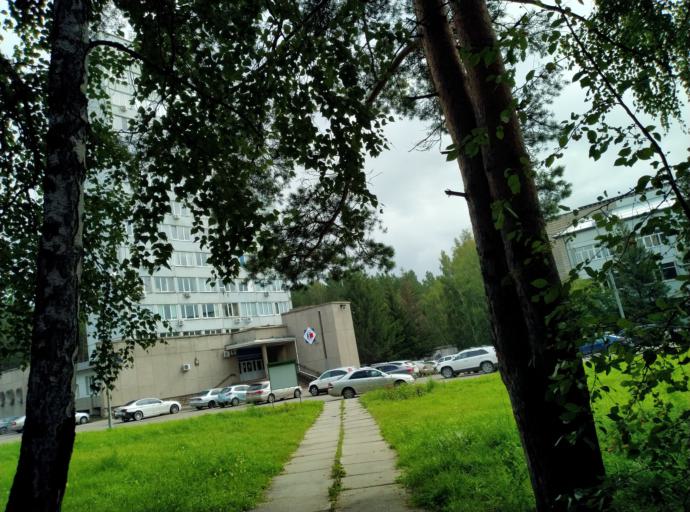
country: RU
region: Krasnoyarskiy
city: Krasnoyarsk
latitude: 55.9919
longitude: 92.7636
